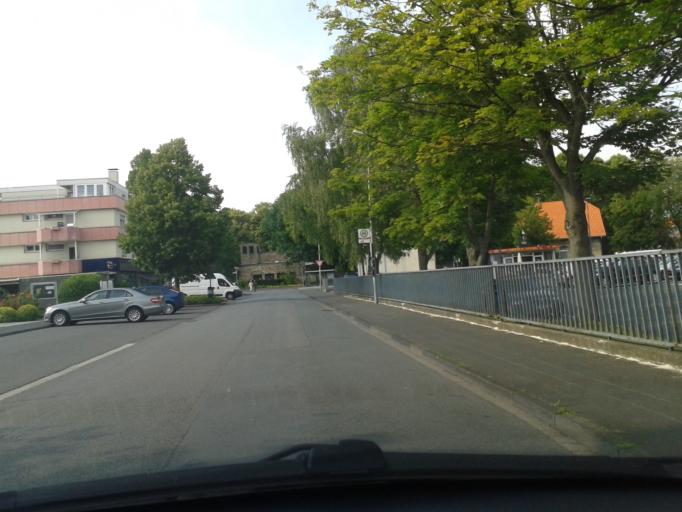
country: DE
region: North Rhine-Westphalia
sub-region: Regierungsbezirk Detmold
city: Paderborn
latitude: 51.7149
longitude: 8.7297
